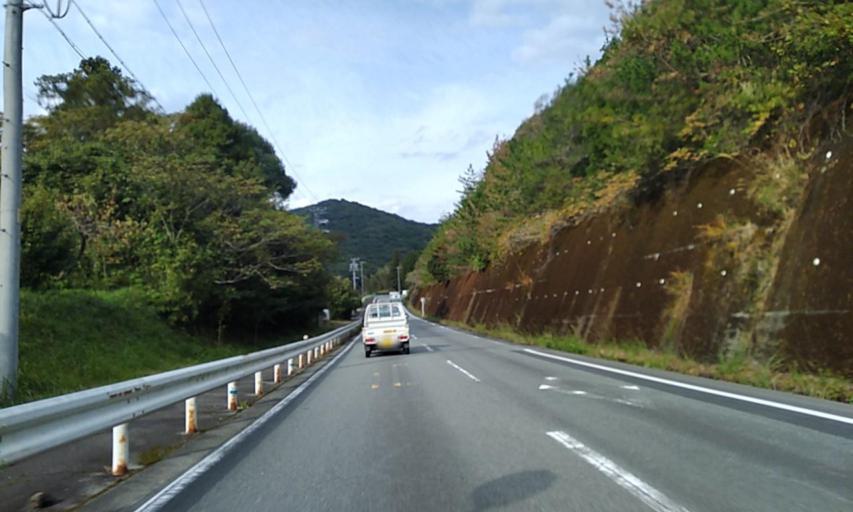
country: JP
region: Mie
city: Ise
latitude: 34.2961
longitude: 136.6021
